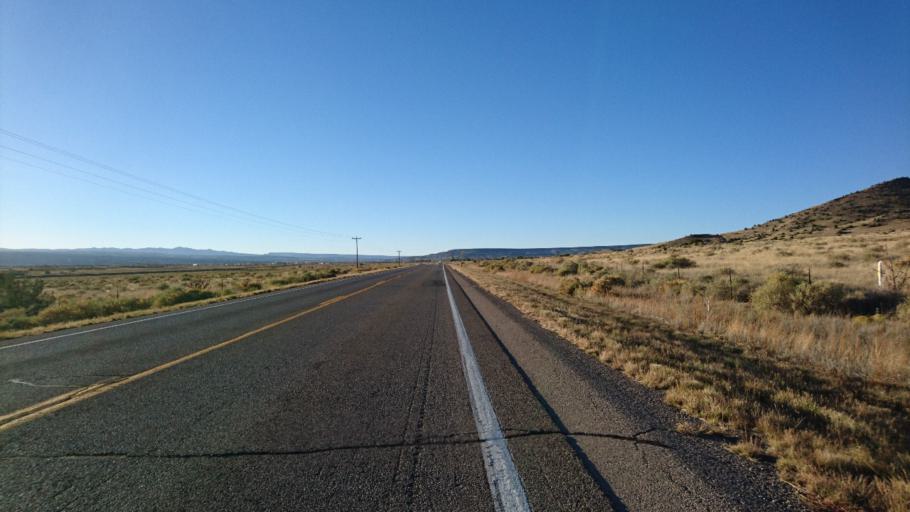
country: US
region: New Mexico
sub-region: Cibola County
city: Grants
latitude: 35.1164
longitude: -107.7879
